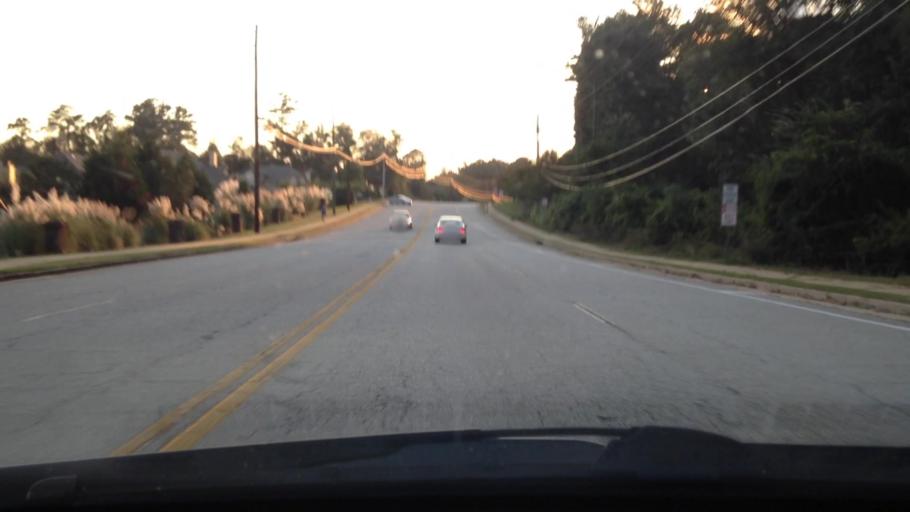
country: US
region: Alabama
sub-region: Russell County
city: Phenix City
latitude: 32.5565
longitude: -84.9770
